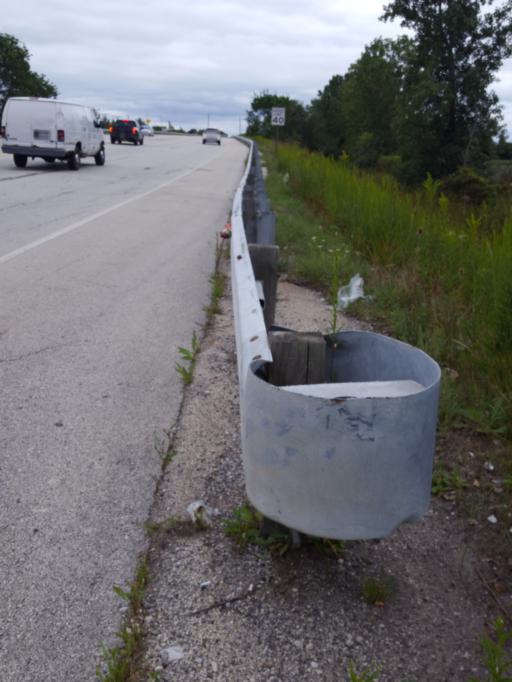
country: US
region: Illinois
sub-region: Lake County
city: Deerfield
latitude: 42.1521
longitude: -87.8483
